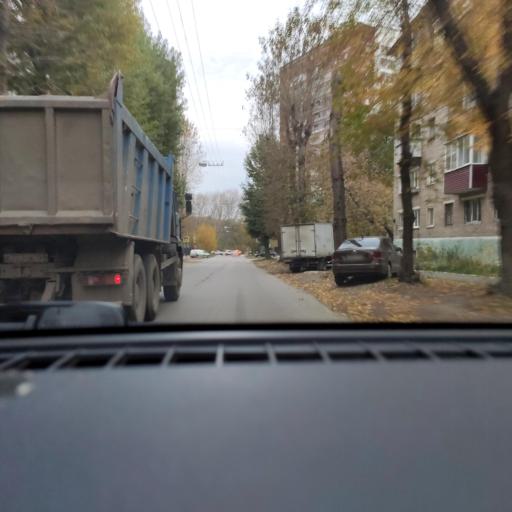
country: RU
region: Perm
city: Kondratovo
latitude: 57.9783
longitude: 56.1751
